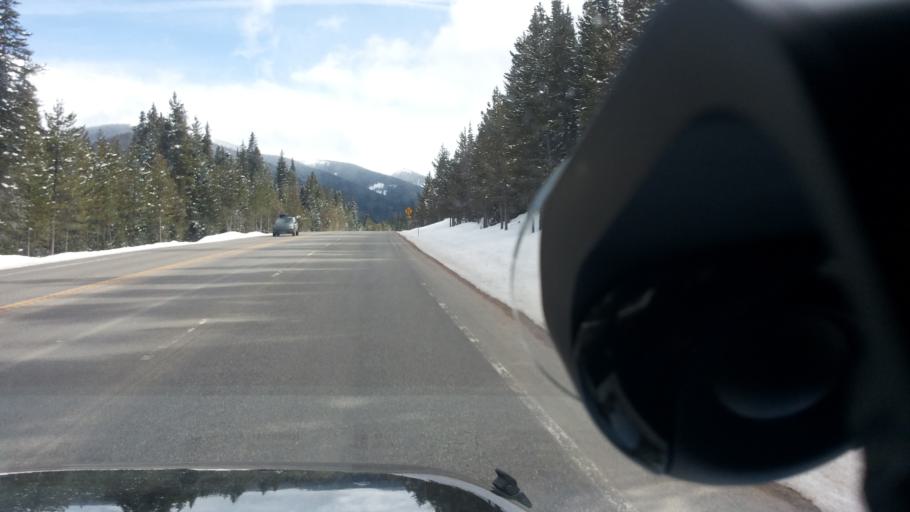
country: US
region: Colorado
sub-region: Grand County
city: Fraser
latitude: 39.8676
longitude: -105.7502
